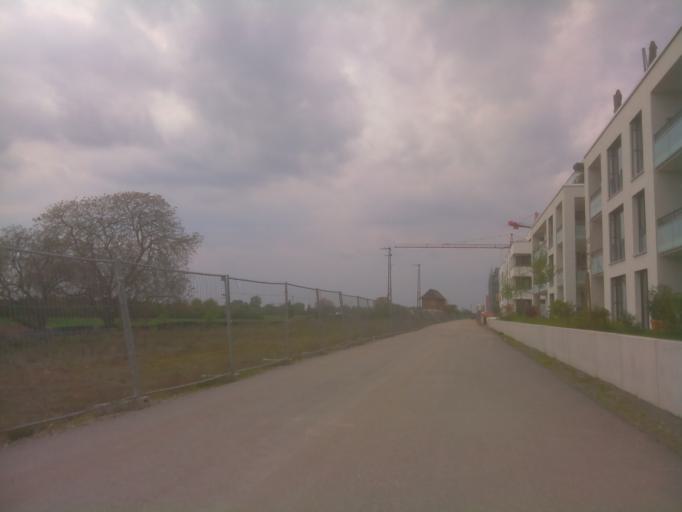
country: DE
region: Baden-Wuerttemberg
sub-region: Karlsruhe Region
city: Heidelberg
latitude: 49.4016
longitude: 8.6645
